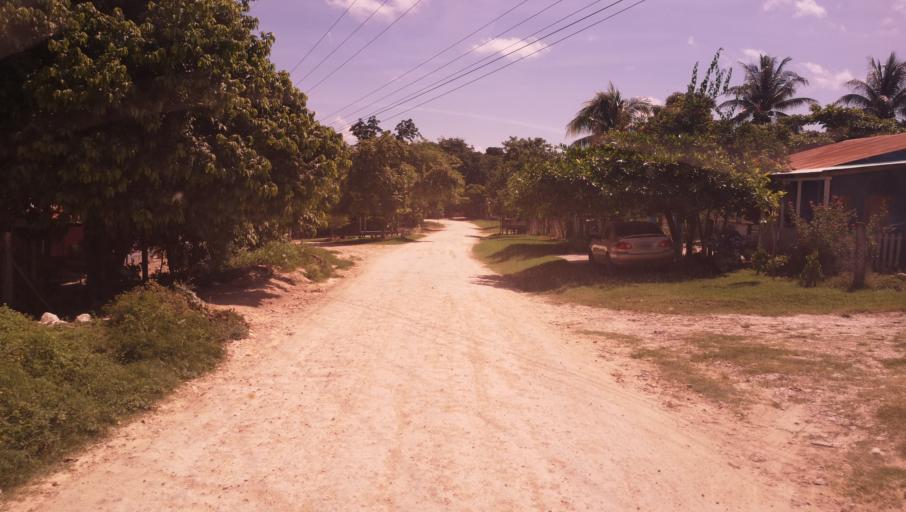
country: GT
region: Peten
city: Melchor de Mencos
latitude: 16.9742
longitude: -89.2641
